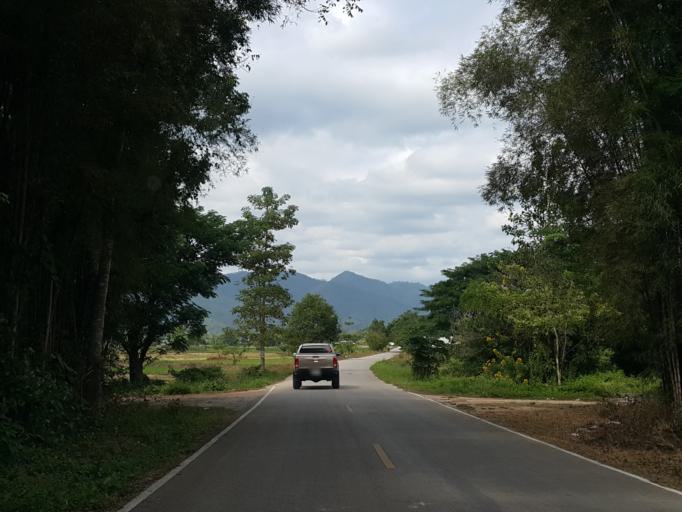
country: TH
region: Lampang
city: Chae Hom
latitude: 18.5510
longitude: 99.4606
